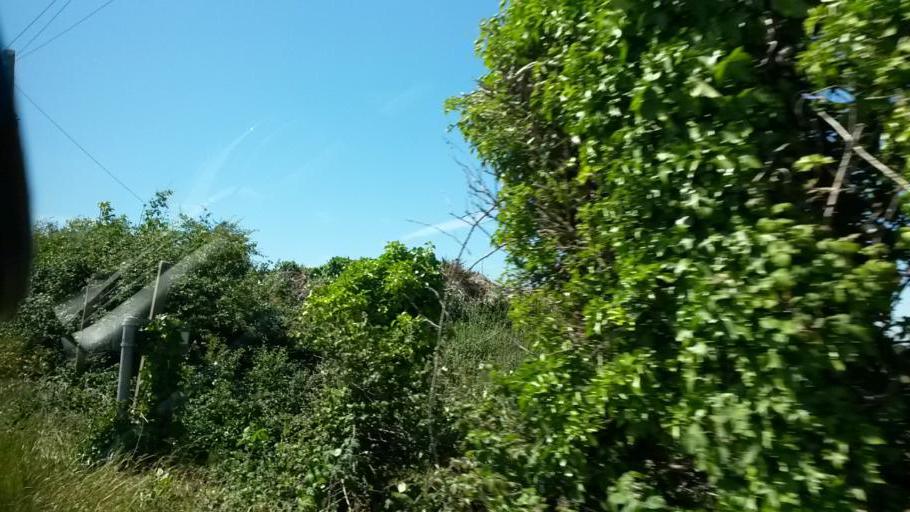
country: IE
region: Leinster
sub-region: Dublin City
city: Finglas
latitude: 53.4338
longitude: -6.2990
